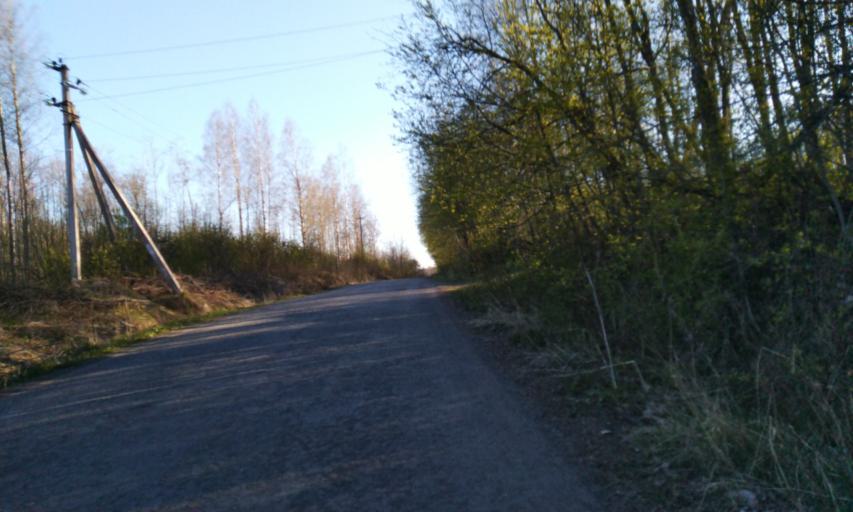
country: RU
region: Leningrad
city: Toksovo
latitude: 60.1465
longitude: 30.5778
